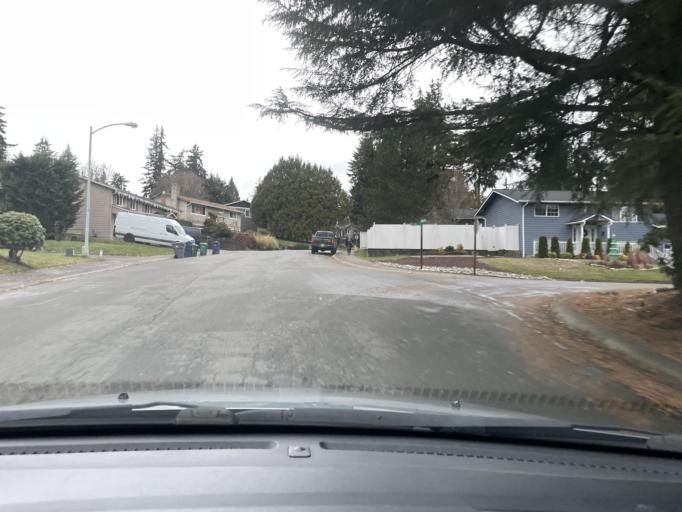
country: US
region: Washington
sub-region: King County
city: Kingsgate
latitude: 47.7202
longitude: -122.1790
